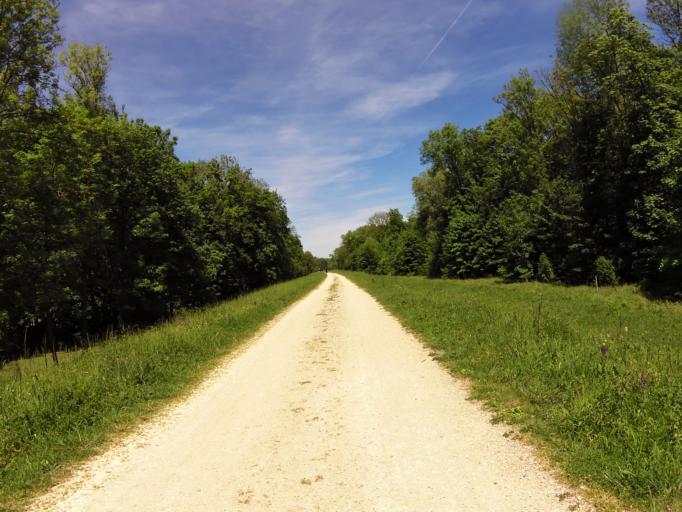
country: DE
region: Bavaria
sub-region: Upper Bavaria
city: Freising
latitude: 48.3901
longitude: 11.7443
